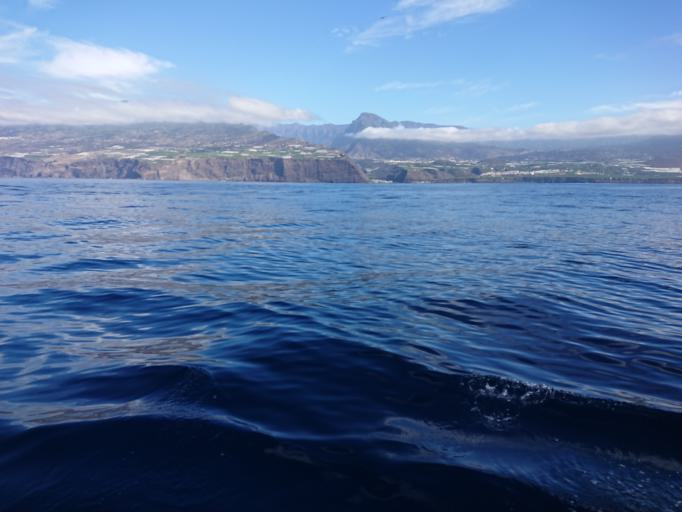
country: ES
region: Canary Islands
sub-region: Provincia de Santa Cruz de Tenerife
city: Tazacorte
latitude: 28.6265
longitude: -17.9948
